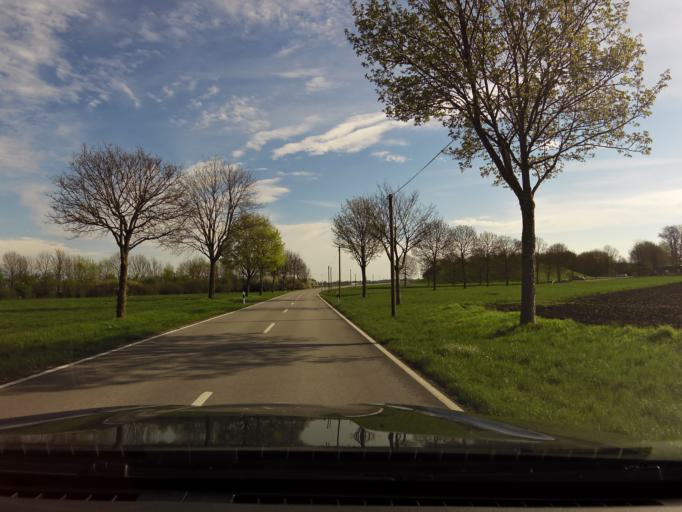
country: DE
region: Bavaria
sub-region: Upper Bavaria
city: Hallbergmoos
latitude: 48.3392
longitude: 11.7923
